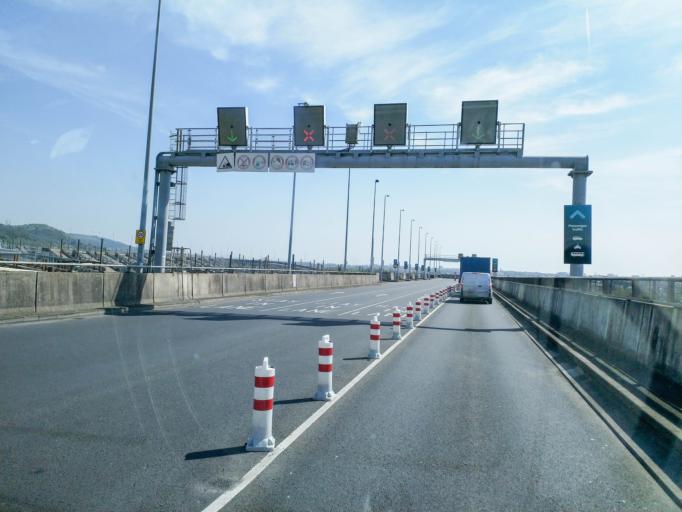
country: GB
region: England
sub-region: Kent
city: Hawkinge
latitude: 51.0969
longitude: 1.1342
